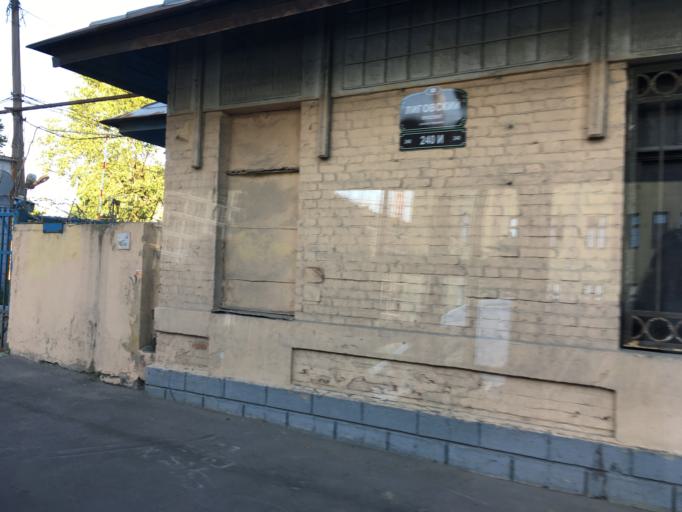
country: RU
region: St.-Petersburg
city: Centralniy
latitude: 59.9043
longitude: 30.3422
